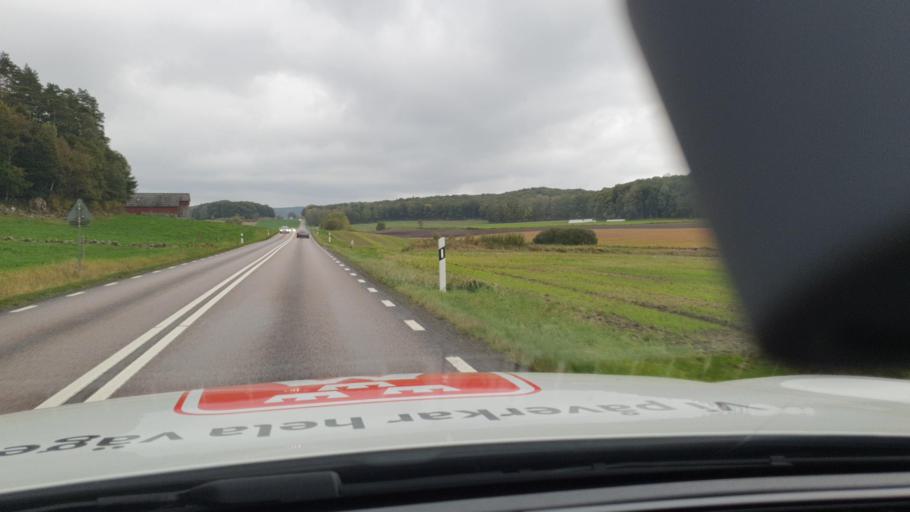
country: SE
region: Halland
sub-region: Falkenbergs Kommun
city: Falkenberg
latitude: 57.0445
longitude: 12.6054
